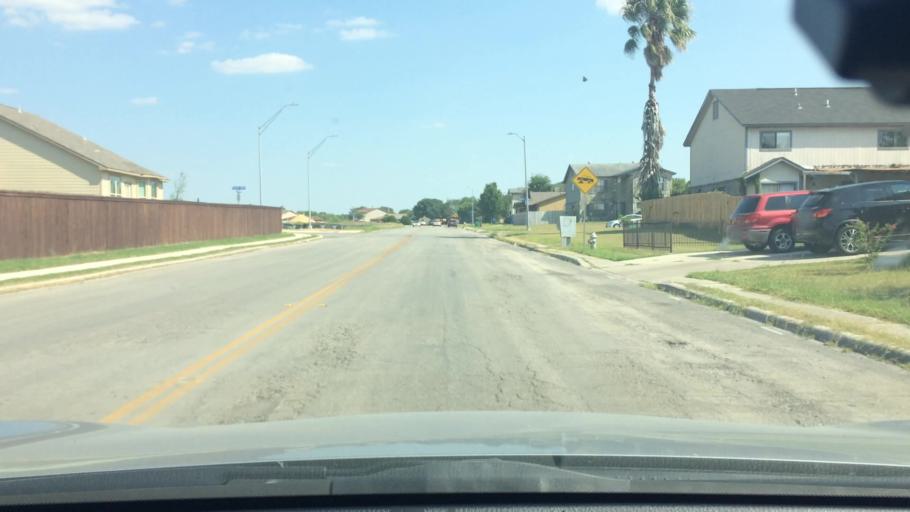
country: US
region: Texas
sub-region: Bexar County
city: Kirby
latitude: 29.4709
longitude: -98.3749
